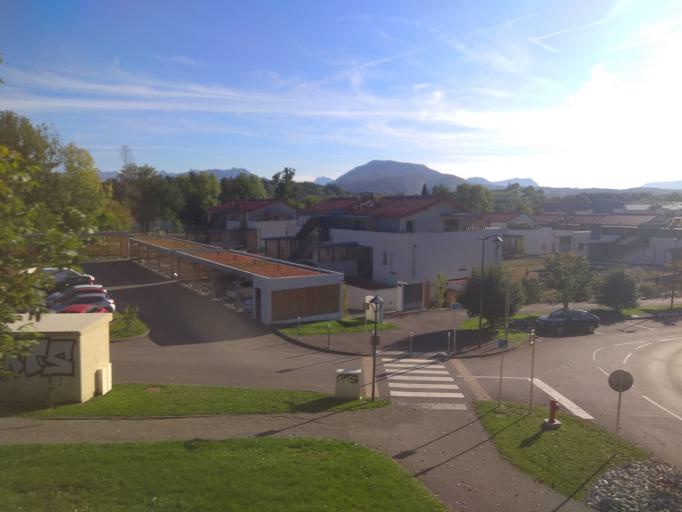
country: FR
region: Rhone-Alpes
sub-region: Departement de la Haute-Savoie
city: Pringy
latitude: 45.9426
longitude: 6.1417
